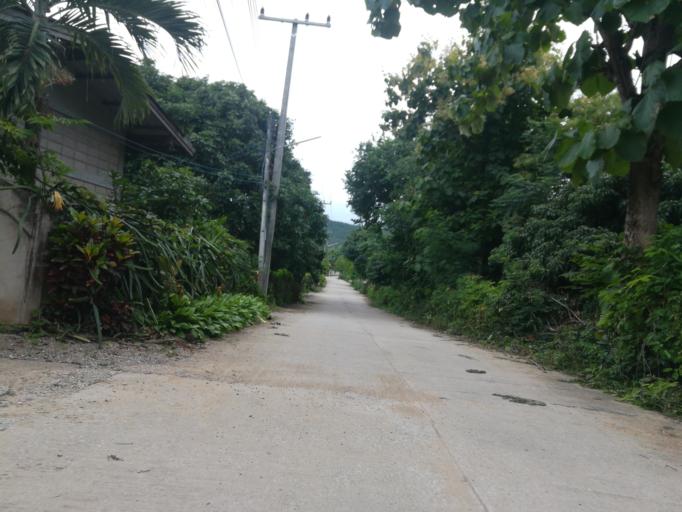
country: TH
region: Chiang Mai
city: Chom Thong
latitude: 18.4045
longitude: 98.6507
